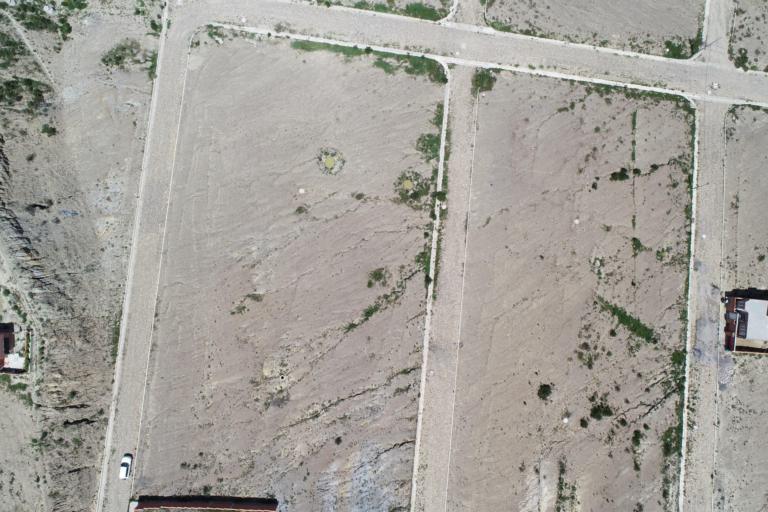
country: BO
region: La Paz
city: La Paz
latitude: -16.5223
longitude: -68.0472
